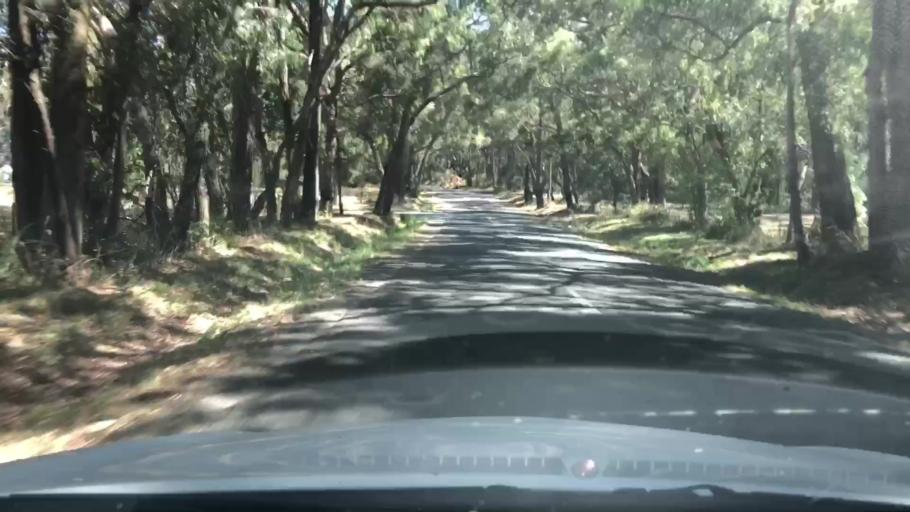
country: AU
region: Victoria
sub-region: Yarra Ranges
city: Macclesfield
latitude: -37.8757
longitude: 145.4781
